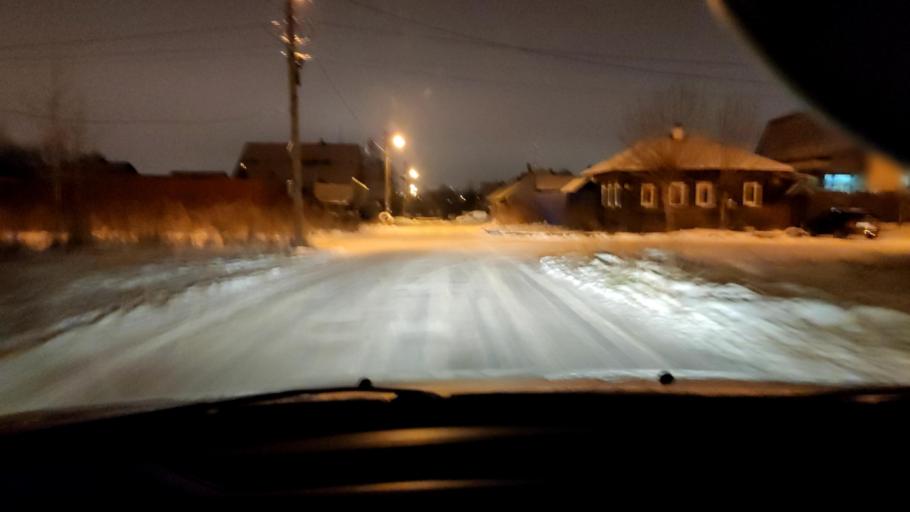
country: RU
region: Perm
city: Perm
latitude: 58.0215
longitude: 56.3295
